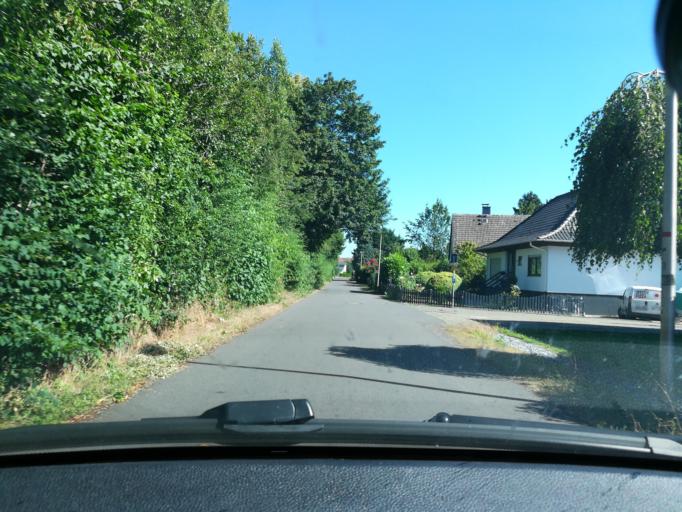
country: DE
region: North Rhine-Westphalia
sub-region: Regierungsbezirk Detmold
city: Minden
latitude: 52.3090
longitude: 8.9387
